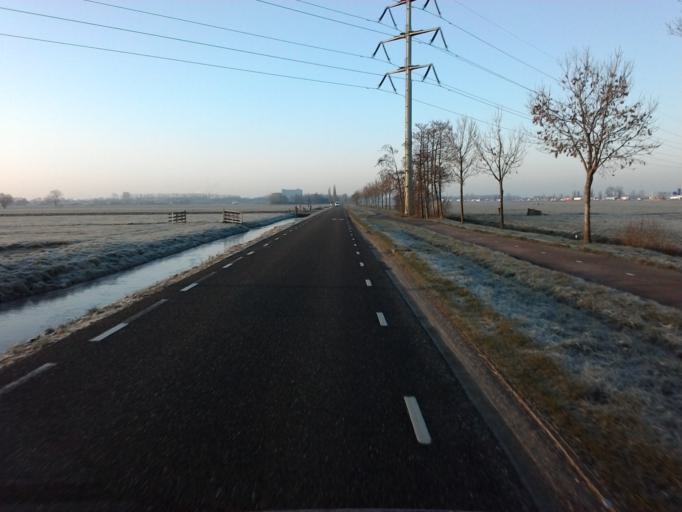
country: NL
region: South Holland
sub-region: Gemeente Gorinchem
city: Gorinchem
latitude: 51.8606
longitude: 4.9643
